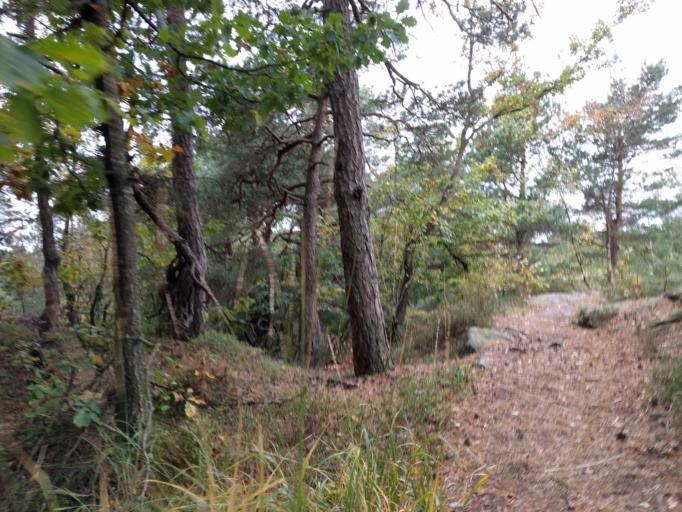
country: NO
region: Vest-Agder
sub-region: Kristiansand
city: Kristiansand
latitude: 58.1444
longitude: 7.9739
